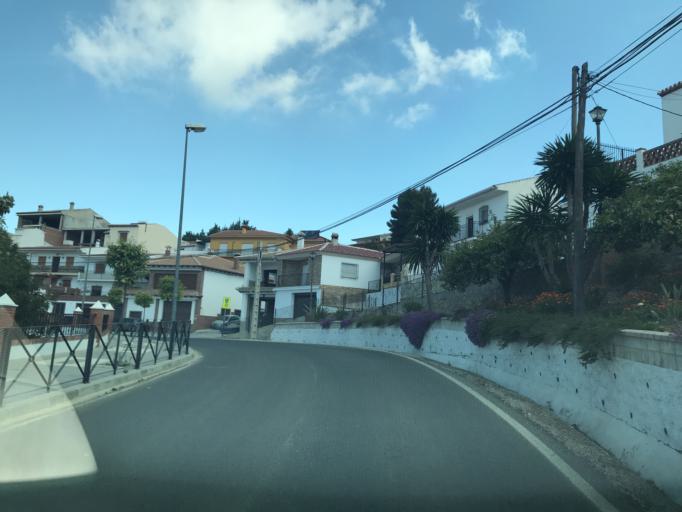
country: ES
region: Andalusia
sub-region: Provincia de Malaga
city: Periana
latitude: 36.9298
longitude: -4.1895
